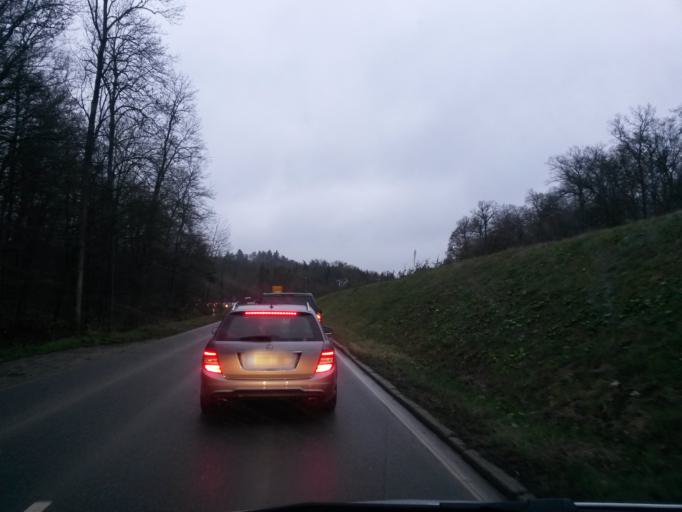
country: DE
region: Baden-Wuerttemberg
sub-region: Regierungsbezirk Stuttgart
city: Sindelfingen
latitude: 48.6970
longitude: 9.0311
